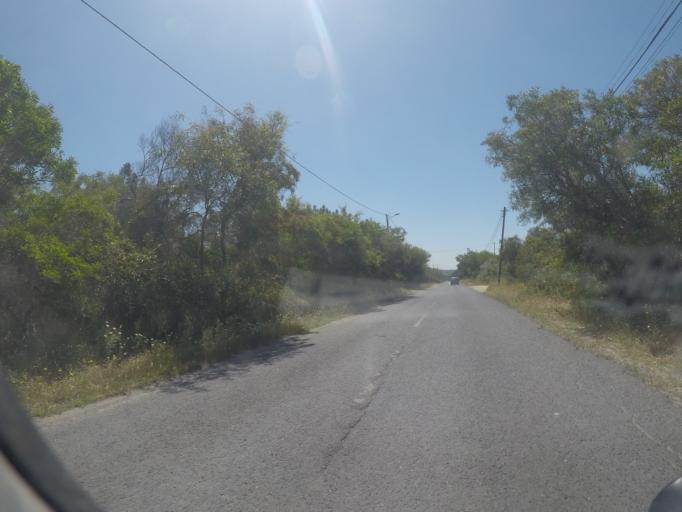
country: PT
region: Setubal
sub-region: Almada
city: Charneca
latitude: 38.6198
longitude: -9.2136
